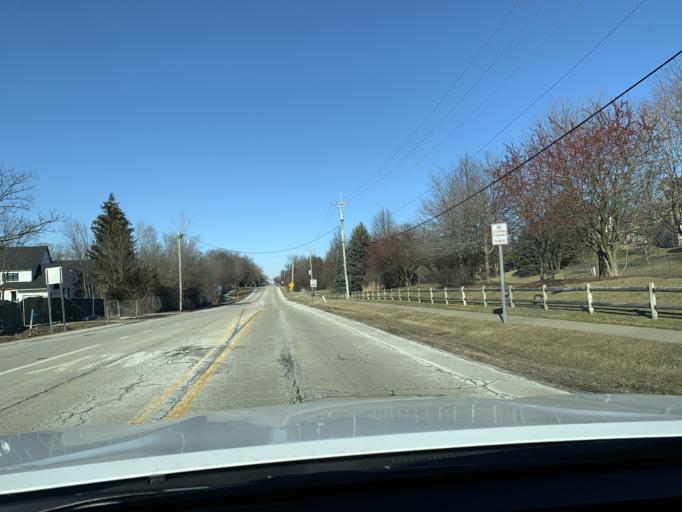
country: US
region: Illinois
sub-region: DuPage County
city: Burr Ridge
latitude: 41.7318
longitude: -87.9149
